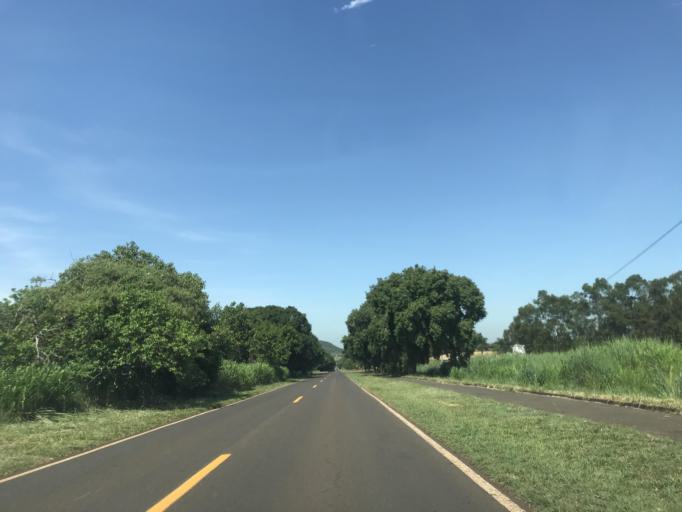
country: BR
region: Parana
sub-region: Terra Rica
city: Terra Rica
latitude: -22.7582
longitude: -52.6317
